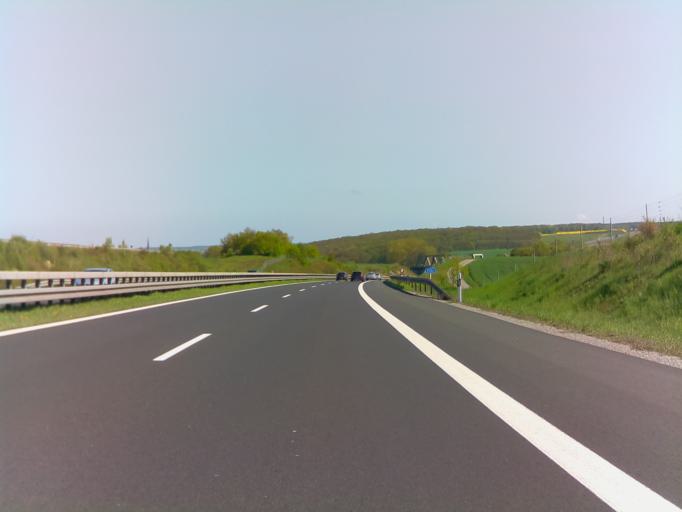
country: DE
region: Bavaria
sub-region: Regierungsbezirk Unterfranken
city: Euerbach
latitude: 50.0727
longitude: 10.1468
